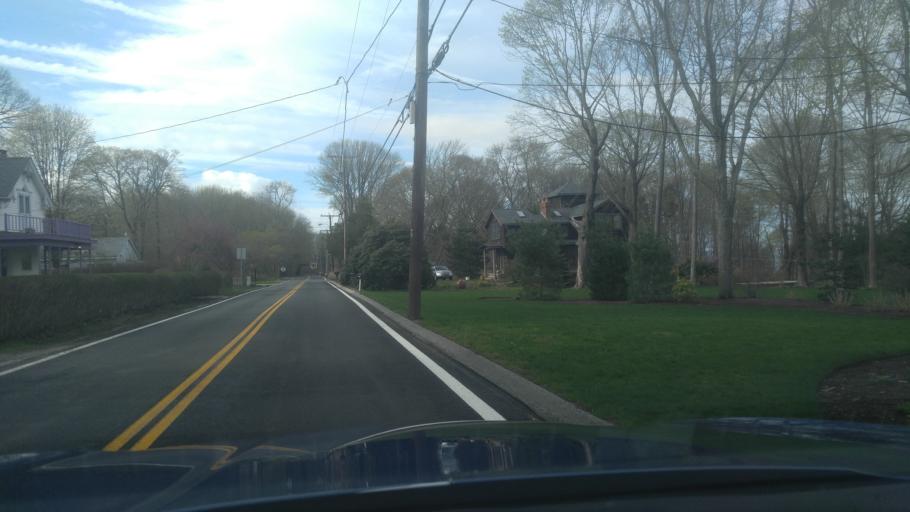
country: US
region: Rhode Island
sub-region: Newport County
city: Jamestown
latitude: 41.5634
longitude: -71.3646
